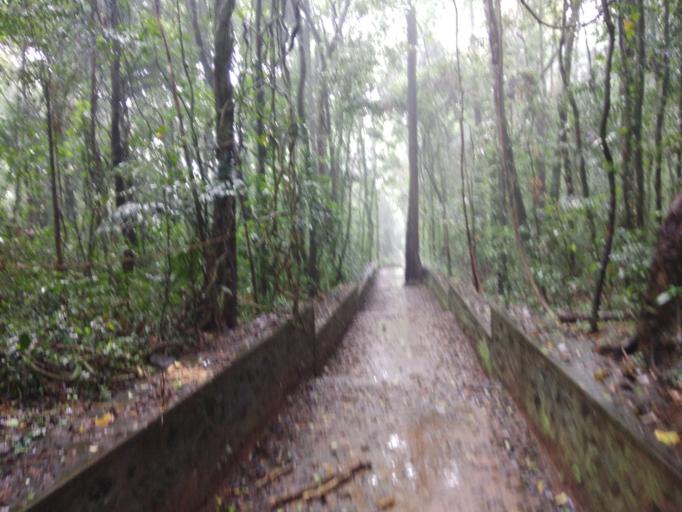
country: IN
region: Kerala
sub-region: Ernakulam
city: Perumpavur
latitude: 10.1086
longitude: 76.5010
